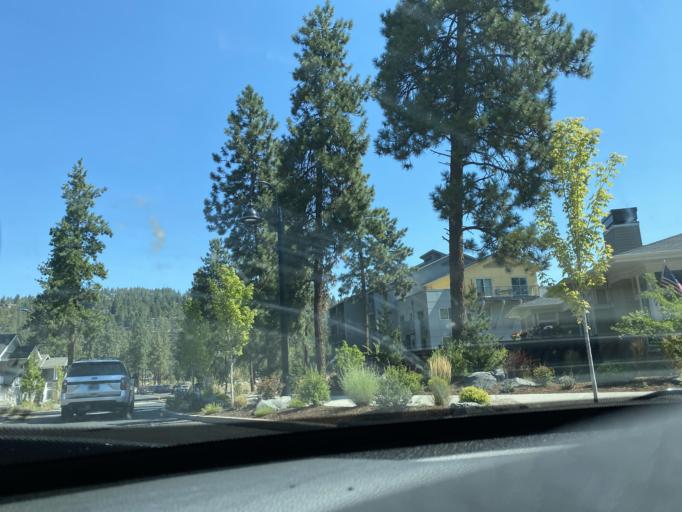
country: US
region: Oregon
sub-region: Deschutes County
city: Bend
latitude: 44.0620
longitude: -121.3460
